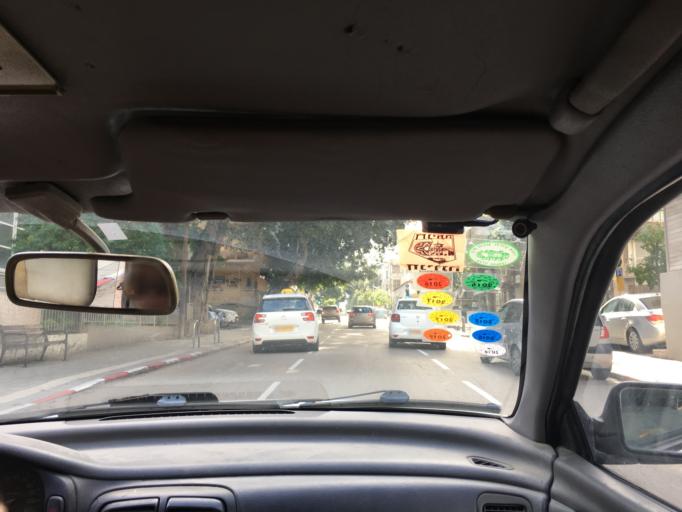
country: IL
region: Tel Aviv
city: Tel Aviv
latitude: 32.0716
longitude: 34.7825
